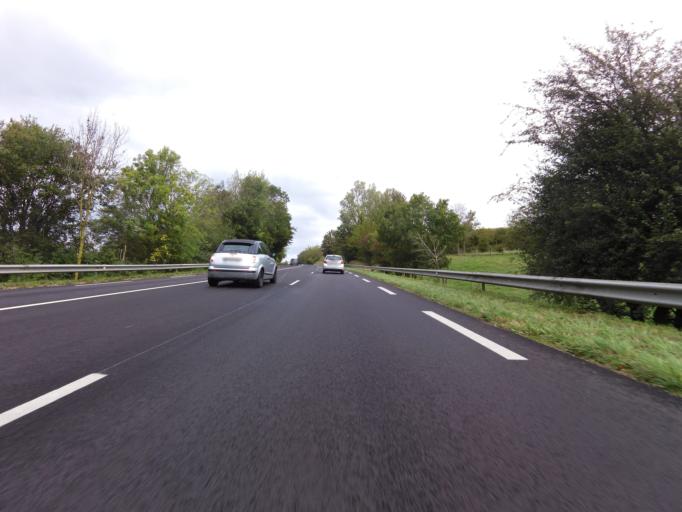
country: FR
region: Haute-Normandie
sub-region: Departement de la Seine-Maritime
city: Criel-sur-Mer
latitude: 50.0120
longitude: 1.3227
